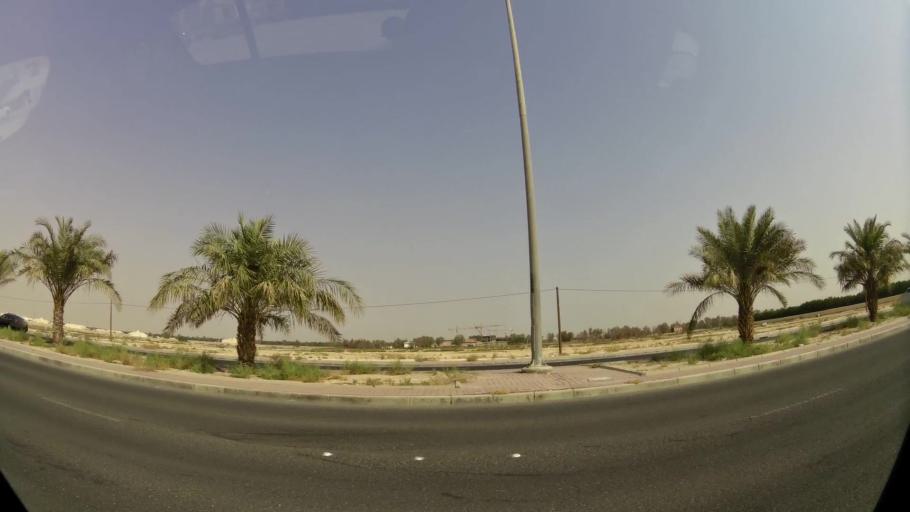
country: KW
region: Muhafazat al Jahra'
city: Al Jahra'
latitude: 29.3245
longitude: 47.7265
